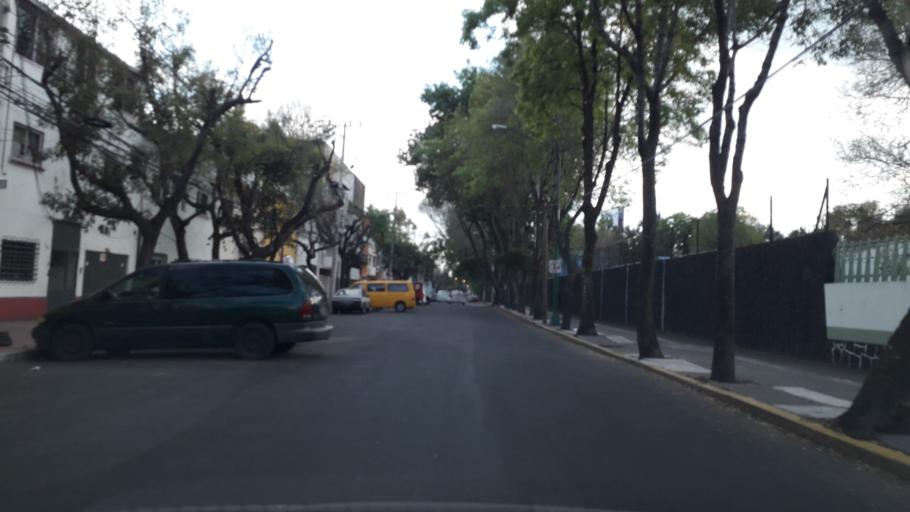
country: MX
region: Mexico City
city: Mexico City
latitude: 19.4054
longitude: -99.1340
